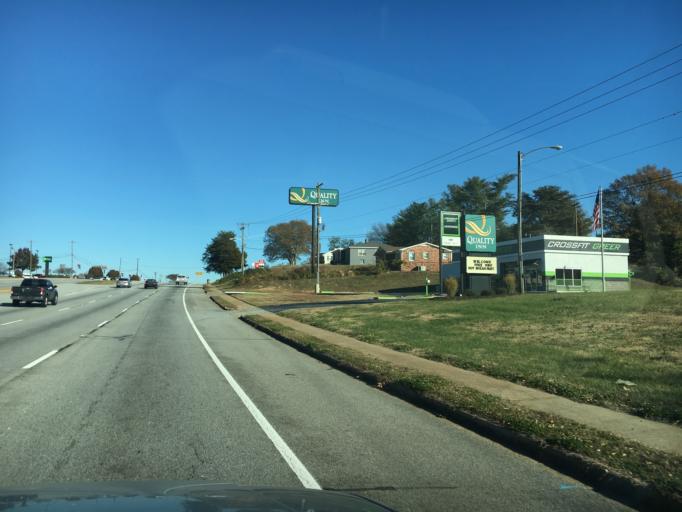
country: US
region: South Carolina
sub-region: Greenville County
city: Greer
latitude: 34.9479
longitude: -82.2417
